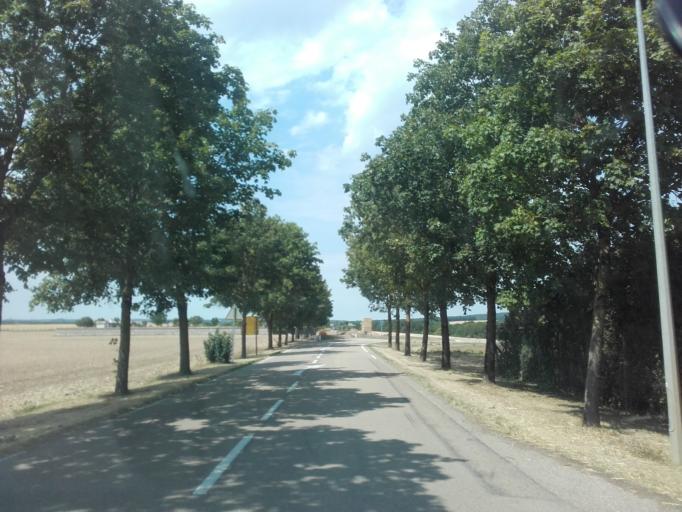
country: FR
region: Bourgogne
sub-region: Departement de l'Yonne
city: Chablis
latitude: 47.7297
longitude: 3.8518
